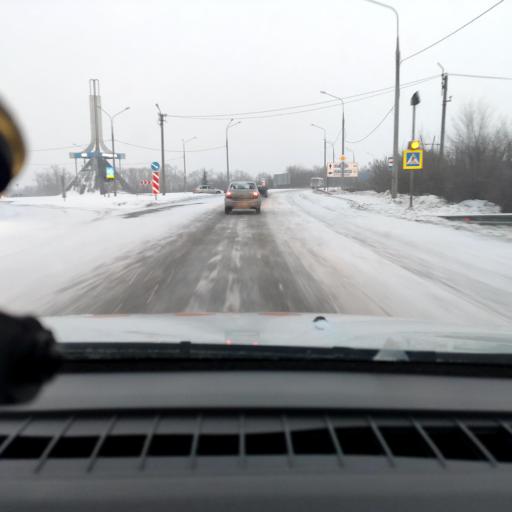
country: RU
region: Samara
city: Otradnyy
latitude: 53.3502
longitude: 51.3259
